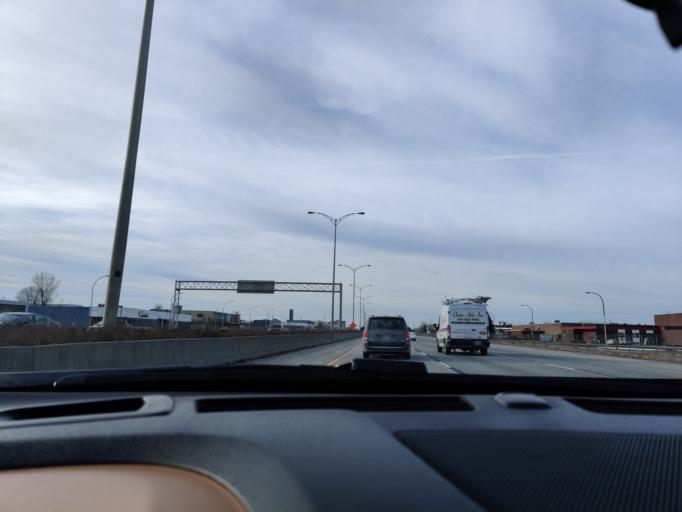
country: CA
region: Quebec
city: Dollard-Des Ormeaux
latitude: 45.4743
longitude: -73.8053
